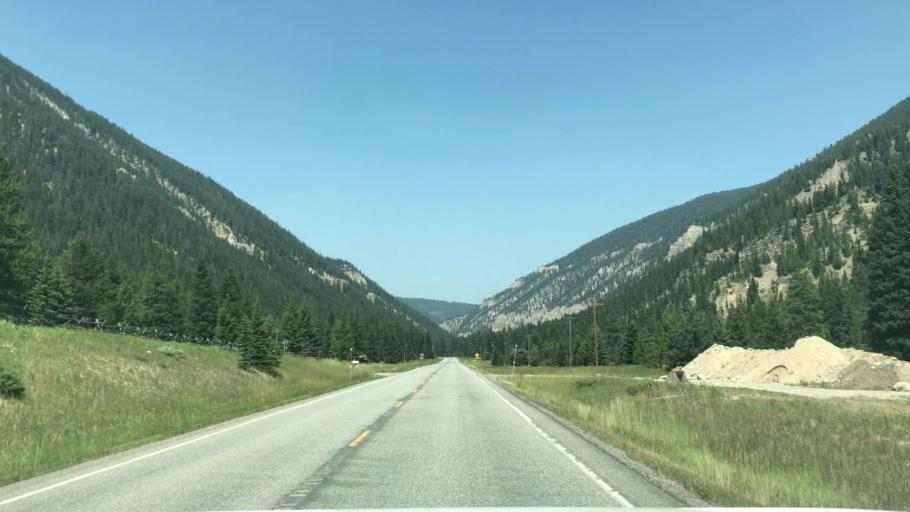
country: US
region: Montana
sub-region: Gallatin County
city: Big Sky
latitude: 45.1196
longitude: -111.2274
